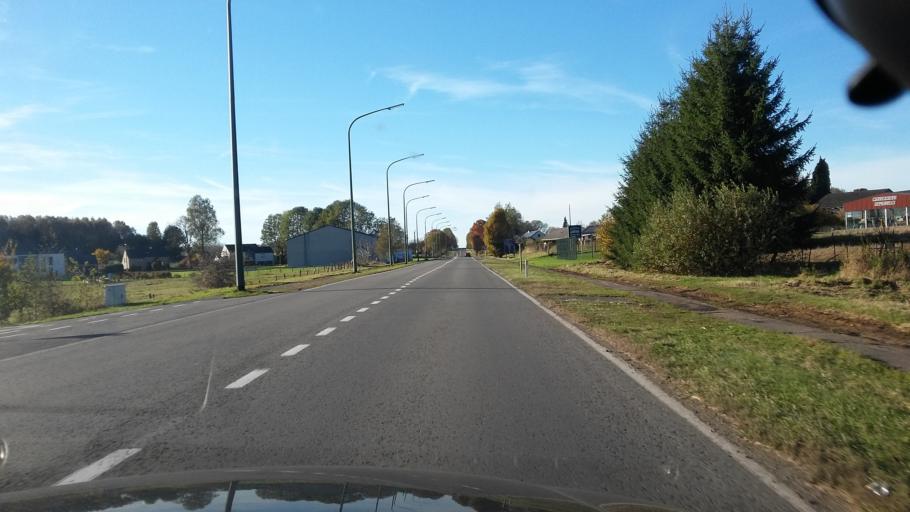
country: BE
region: Wallonia
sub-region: Province du Luxembourg
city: Saint-Leger
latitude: 49.6683
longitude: 5.6663
